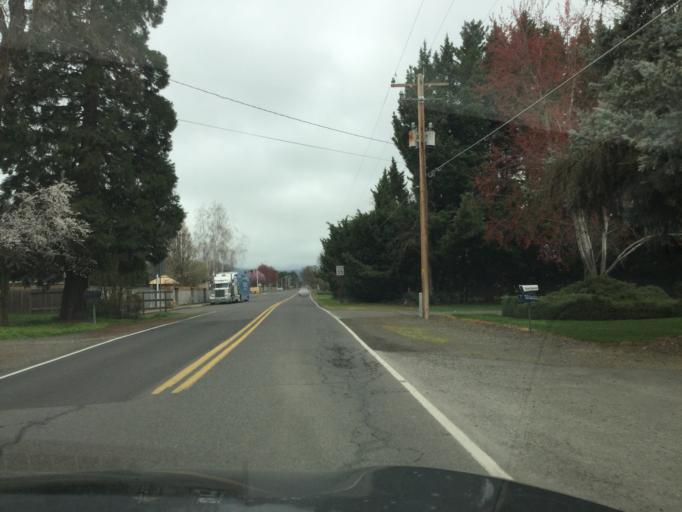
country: US
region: Oregon
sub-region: Jackson County
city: Central Point
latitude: 42.3894
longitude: -122.9264
